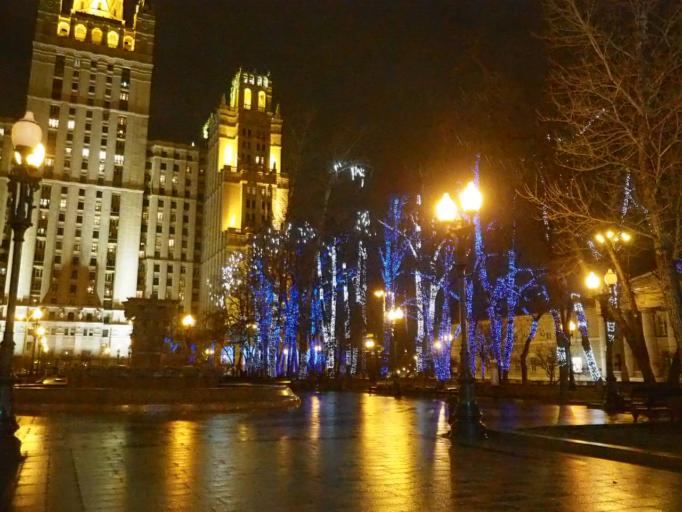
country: RU
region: Moskovskaya
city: Dorogomilovo
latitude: 55.7588
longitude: 37.5831
